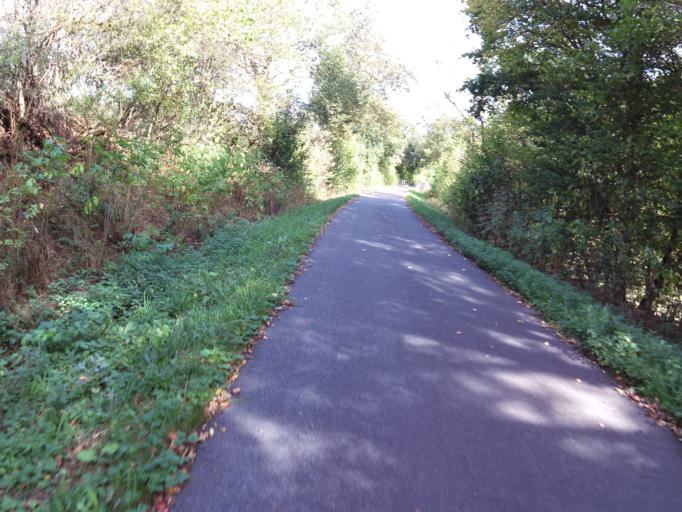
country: DE
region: Rheinland-Pfalz
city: Kickeshausen
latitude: 50.0653
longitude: 6.2480
